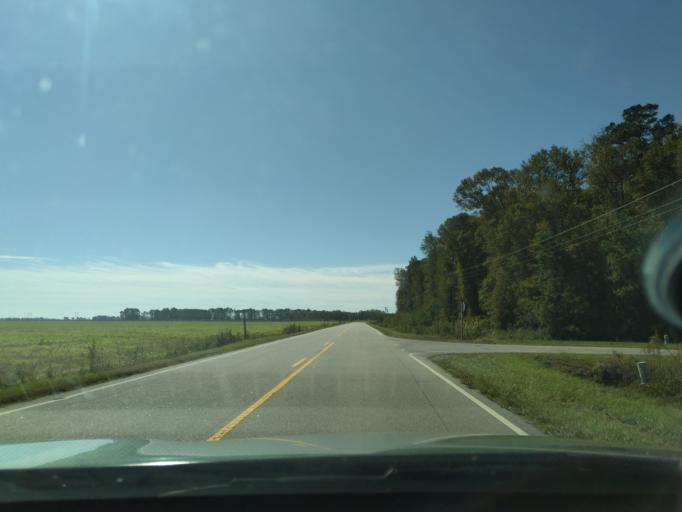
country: US
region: North Carolina
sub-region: Washington County
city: Plymouth
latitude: 35.7465
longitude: -76.7397
